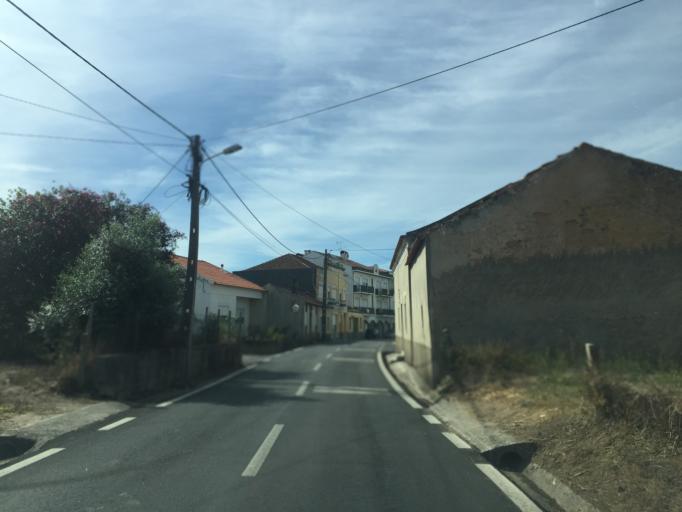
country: PT
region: Coimbra
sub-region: Figueira da Foz
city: Lavos
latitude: 40.0721
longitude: -8.8032
